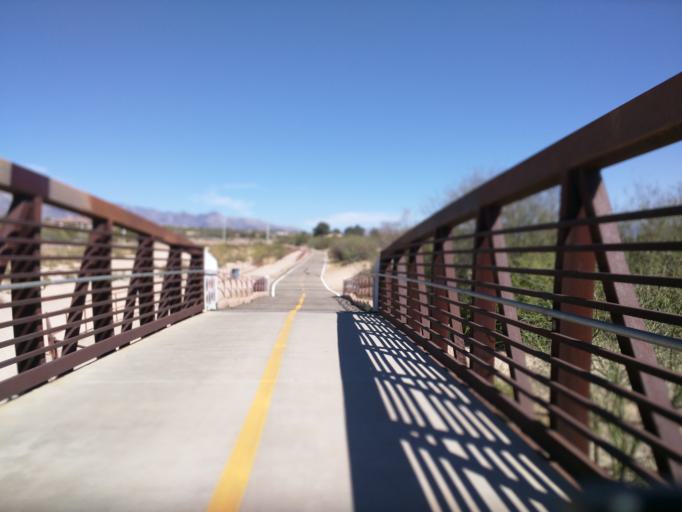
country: US
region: Arizona
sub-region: Pima County
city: Catalina Foothills
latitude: 32.2812
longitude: -110.9376
